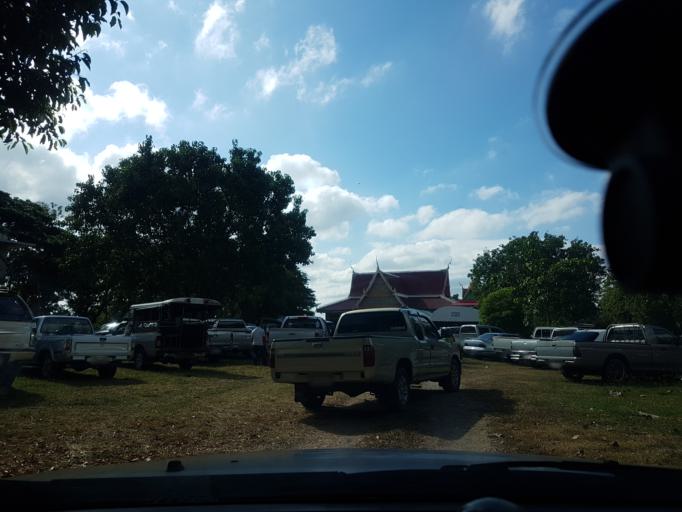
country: TH
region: Lop Buri
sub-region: Amphoe Tha Luang
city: Tha Luang
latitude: 15.0652
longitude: 101.0514
